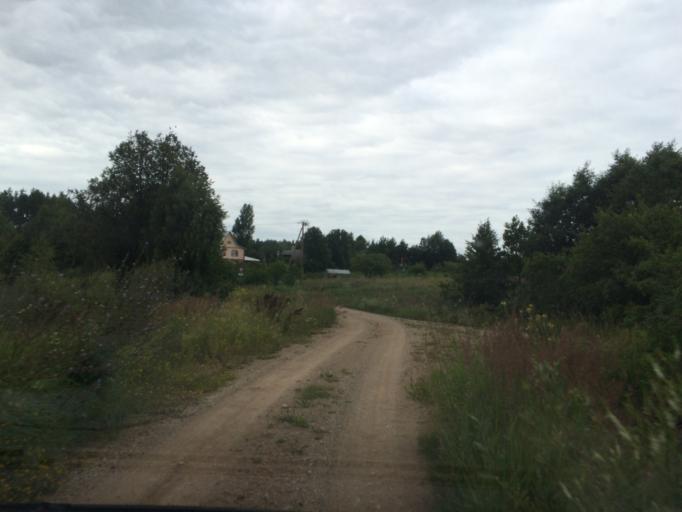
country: LV
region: Rezekne
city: Rezekne
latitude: 56.5880
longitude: 27.4106
